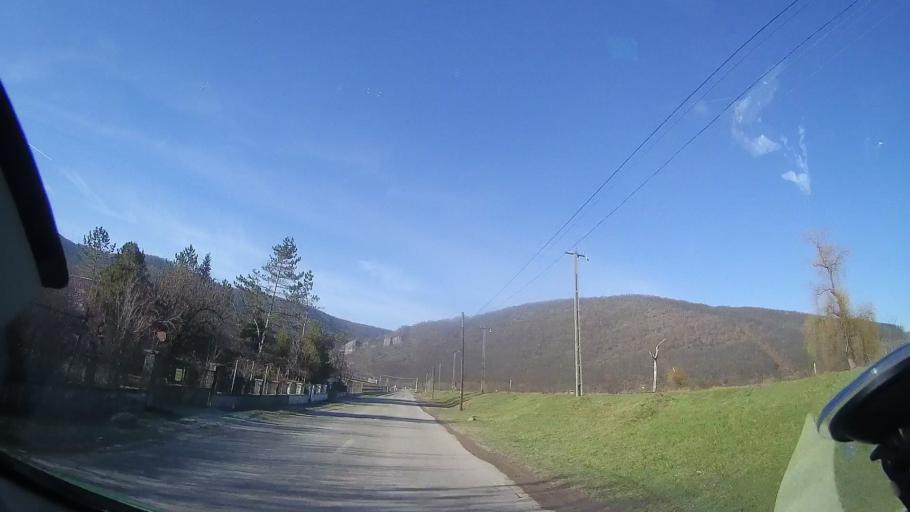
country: RO
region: Bihor
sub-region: Comuna Suncuius
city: Suncuius
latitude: 46.9489
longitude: 22.5358
